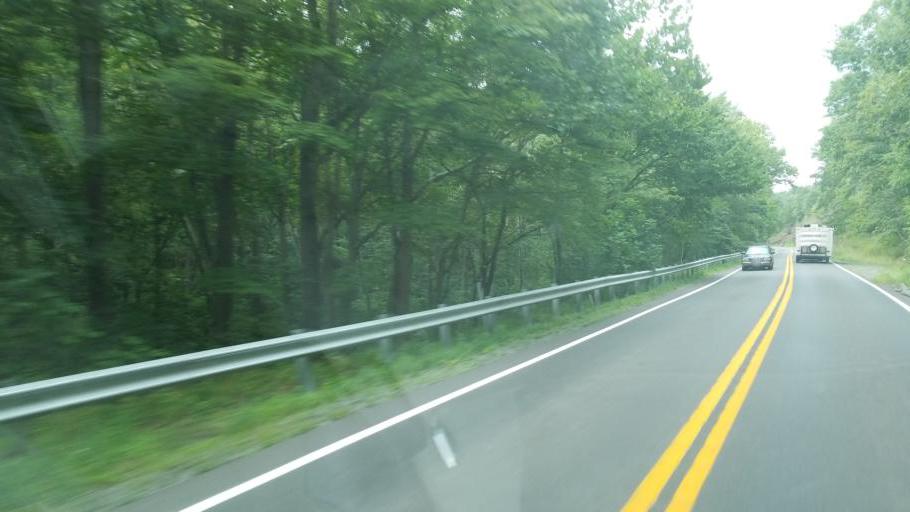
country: US
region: West Virginia
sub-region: Mineral County
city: Fort Ashby
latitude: 39.5424
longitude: -78.5052
